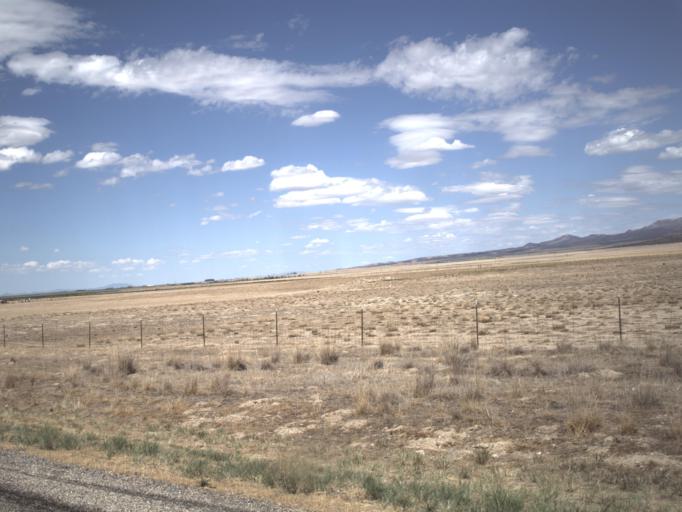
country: US
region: Utah
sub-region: Millard County
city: Fillmore
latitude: 39.1160
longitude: -112.3106
